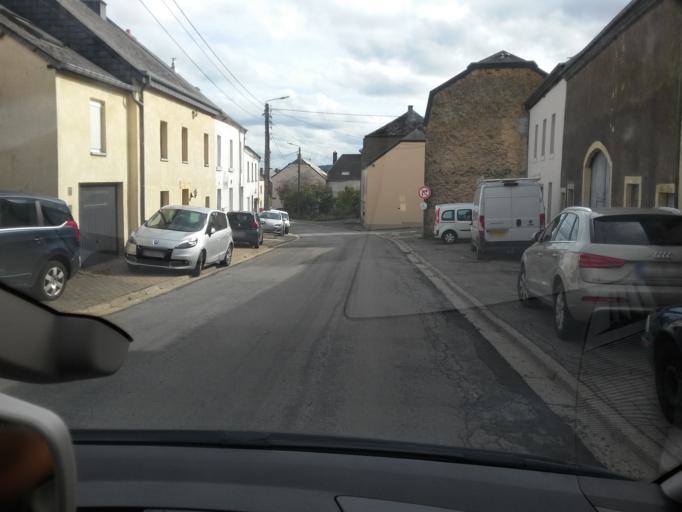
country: BE
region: Wallonia
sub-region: Province du Luxembourg
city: Arlon
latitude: 49.6983
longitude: 5.7656
